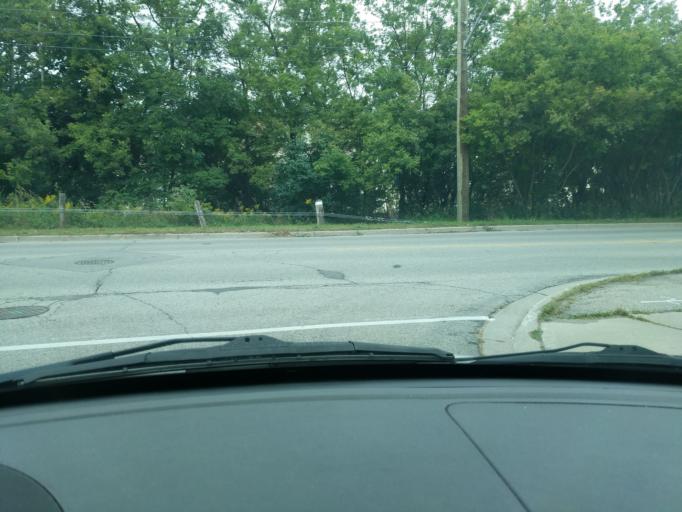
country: CA
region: Ontario
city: Cambridge
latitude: 43.4267
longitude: -80.3201
